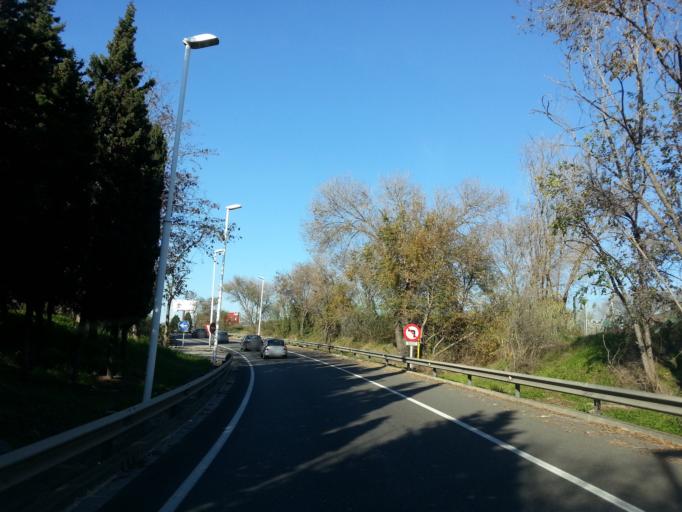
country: ES
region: Catalonia
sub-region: Provincia de Barcelona
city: Sant Adria de Besos
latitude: 41.4270
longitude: 2.2168
